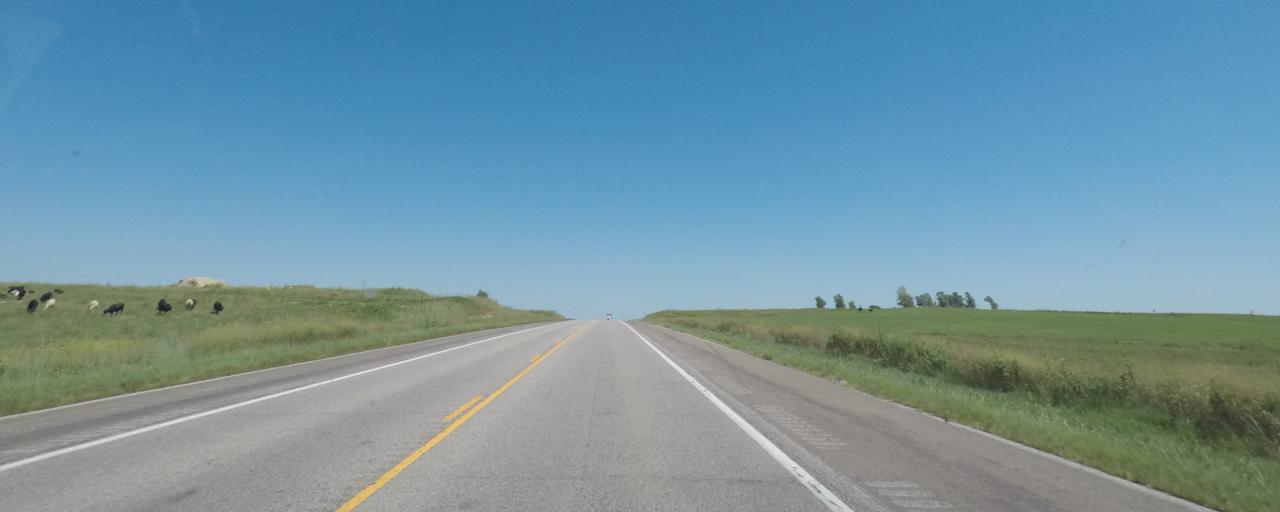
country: US
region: Kansas
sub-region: Chase County
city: Cottonwood Falls
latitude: 38.4055
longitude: -96.4504
